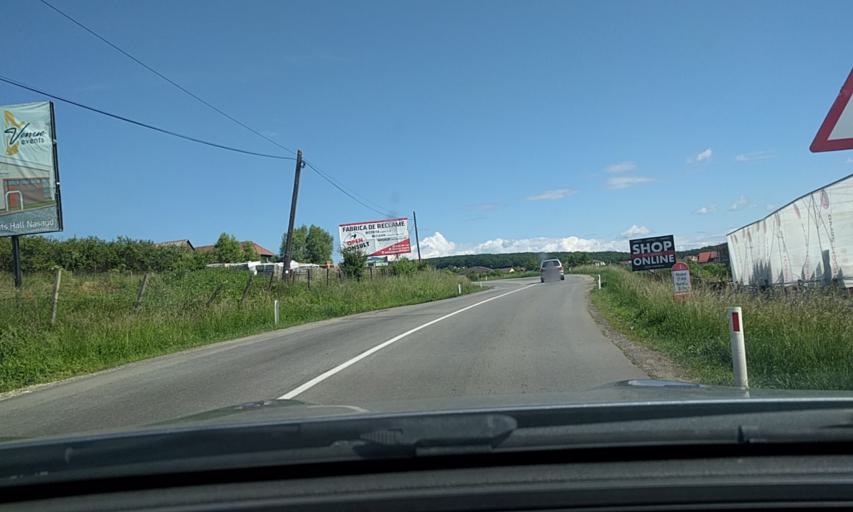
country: RO
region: Bistrita-Nasaud
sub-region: Municipiul Bistrita
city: Unirea
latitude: 47.1564
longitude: 24.5086
